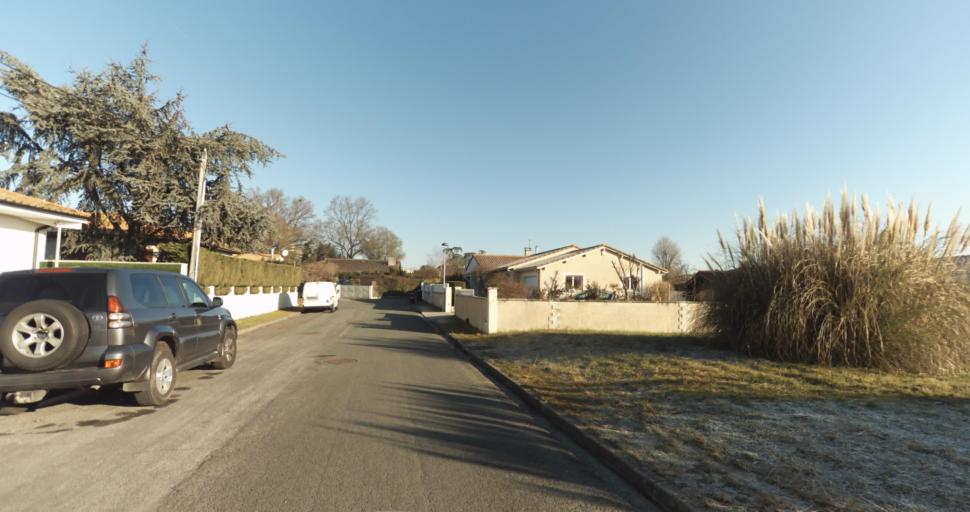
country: FR
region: Aquitaine
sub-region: Departement de la Gironde
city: Bassens
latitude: 44.8894
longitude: -0.5140
